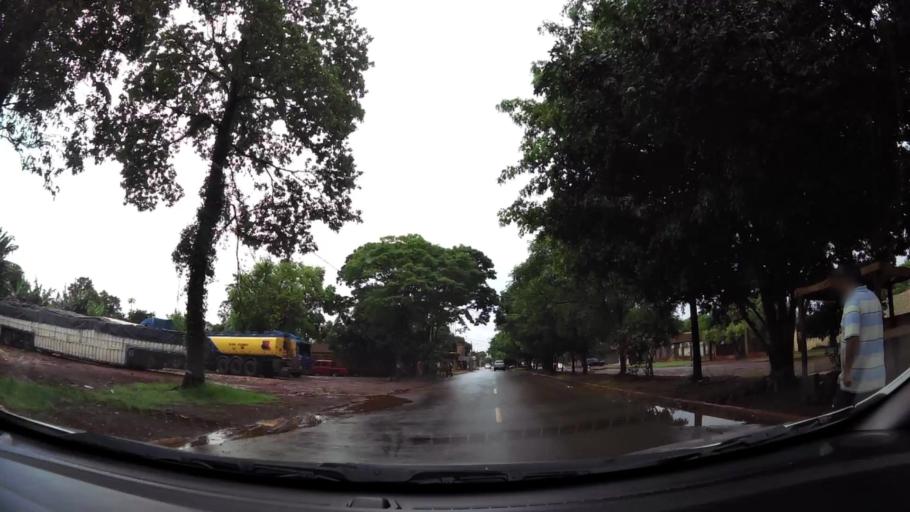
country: PY
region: Alto Parana
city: Presidente Franco
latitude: -25.5221
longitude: -54.6649
